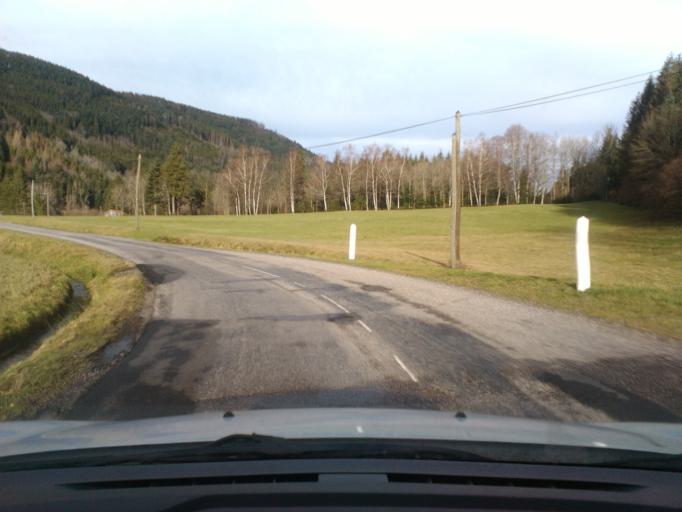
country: FR
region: Lorraine
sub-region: Departement des Vosges
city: Xonrupt-Longemer
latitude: 48.1302
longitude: 6.9571
